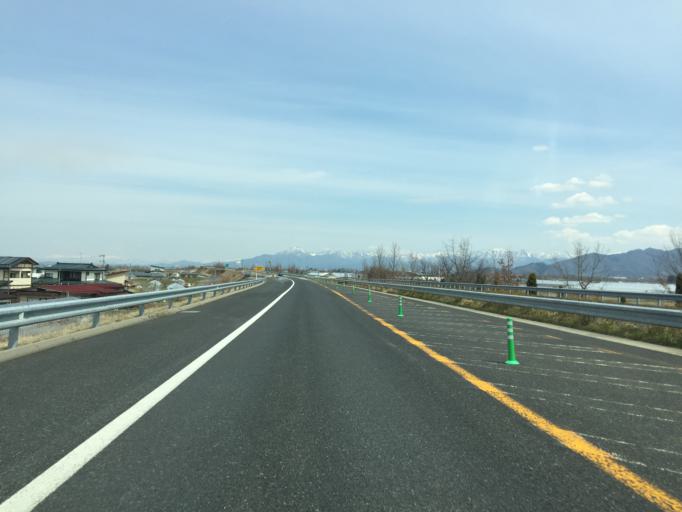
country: JP
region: Yamagata
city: Tendo
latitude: 38.3172
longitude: 140.3228
